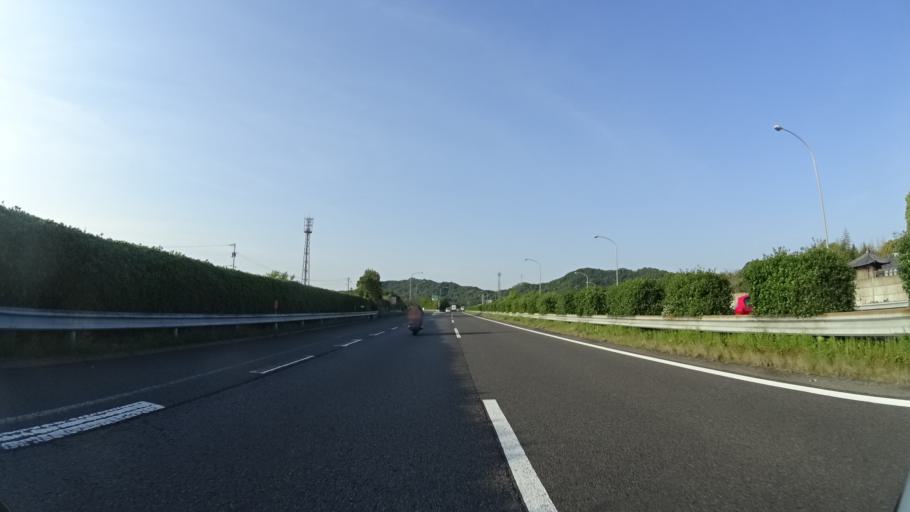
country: JP
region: Kagawa
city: Kan'onjicho
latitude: 34.1461
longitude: 133.7139
